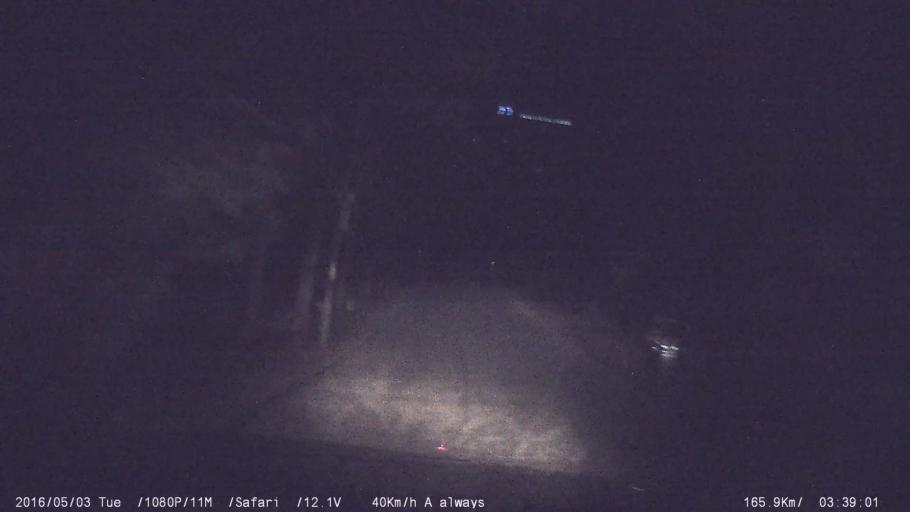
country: IN
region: Kerala
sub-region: Kottayam
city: Palackattumala
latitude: 9.7496
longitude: 76.6096
